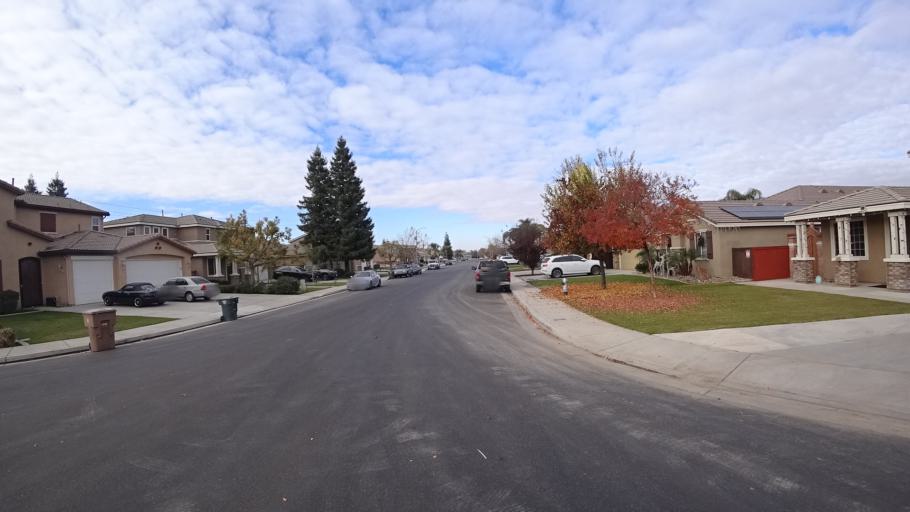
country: US
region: California
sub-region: Kern County
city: Rosedale
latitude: 35.2970
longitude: -119.1332
